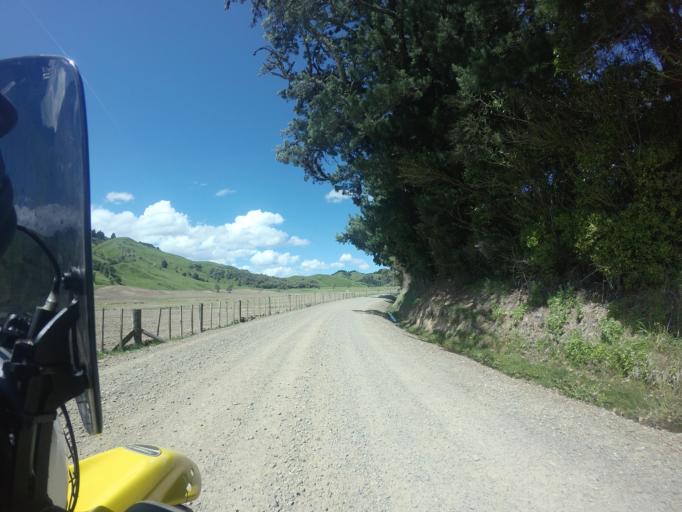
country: NZ
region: Hawke's Bay
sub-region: Wairoa District
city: Wairoa
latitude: -38.9877
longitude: 177.7038
